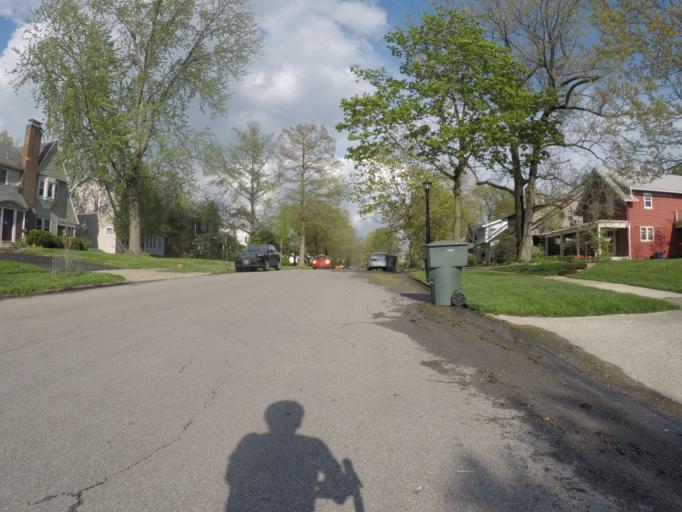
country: US
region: Ohio
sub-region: Franklin County
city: Worthington
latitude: 40.0331
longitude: -83.0092
